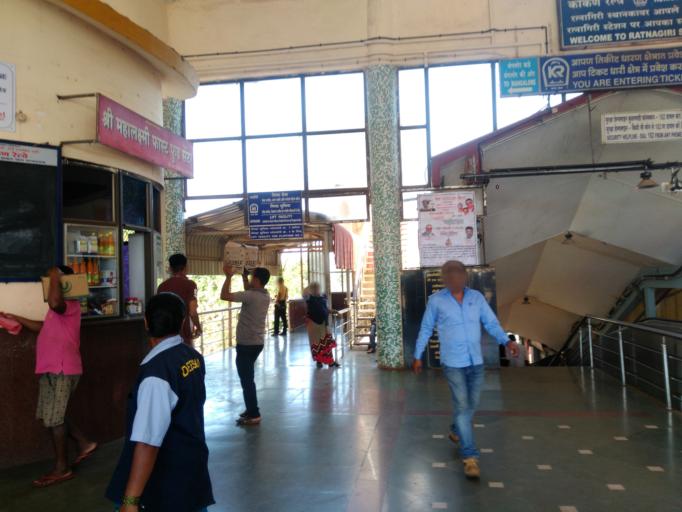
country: IN
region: Maharashtra
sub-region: Ratnagiri
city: Ratnagiri
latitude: 17.0028
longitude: 73.3584
